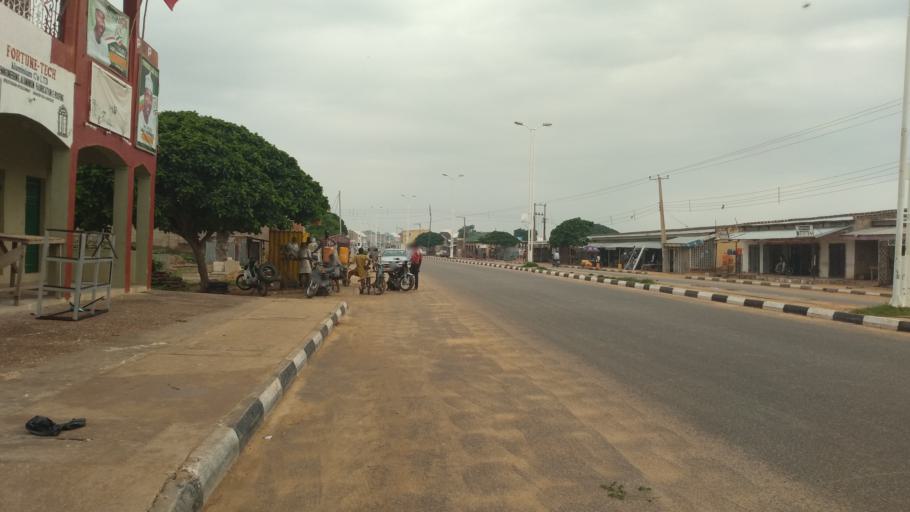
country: NG
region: Katsina
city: Katsina
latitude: 12.9807
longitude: 7.6412
